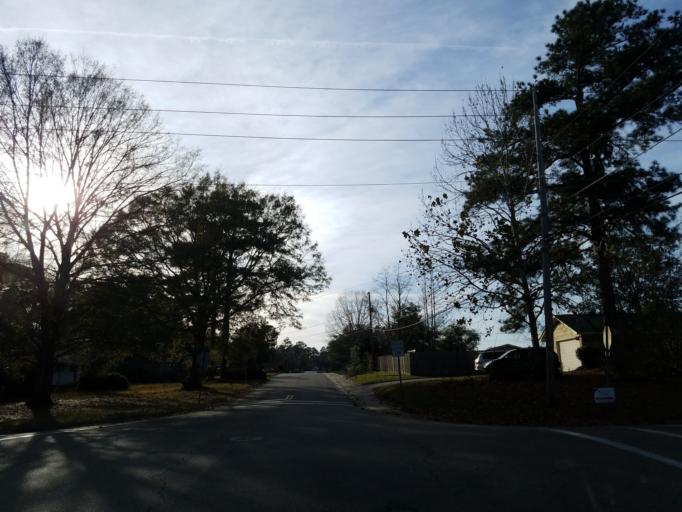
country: US
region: Mississippi
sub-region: Lamar County
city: West Hattiesburg
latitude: 31.3129
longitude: -89.3347
